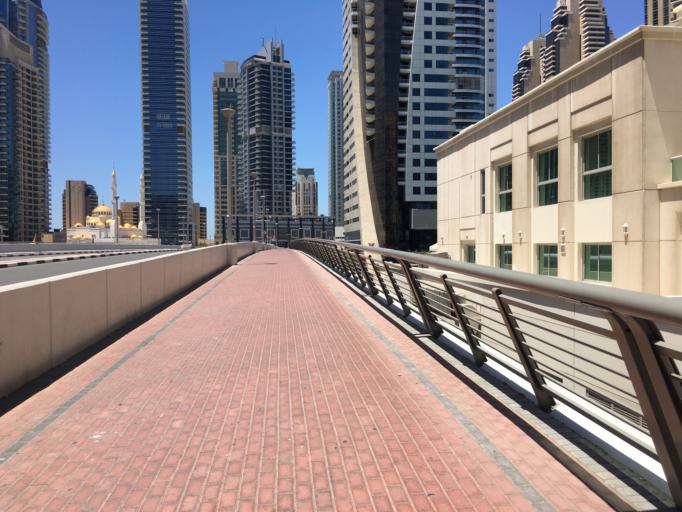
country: AE
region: Dubai
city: Dubai
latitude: 25.0819
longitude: 55.1451
